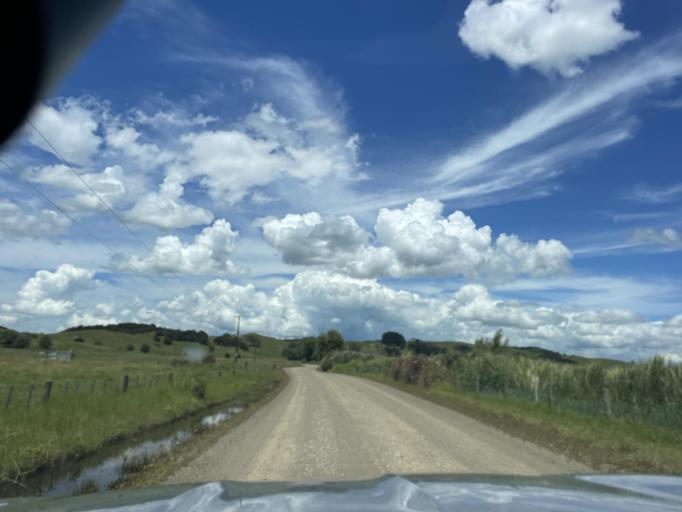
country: NZ
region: Northland
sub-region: Kaipara District
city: Dargaville
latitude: -35.8975
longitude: 173.9162
